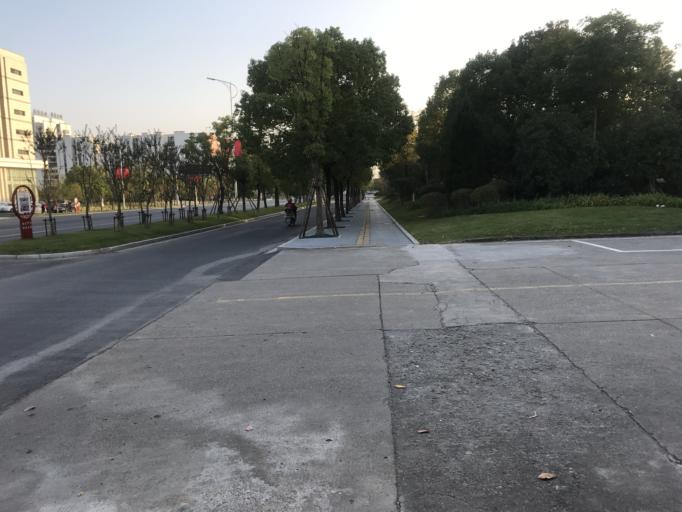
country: CN
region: Anhui Sheng
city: Xintan
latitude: 29.7759
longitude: 118.2587
